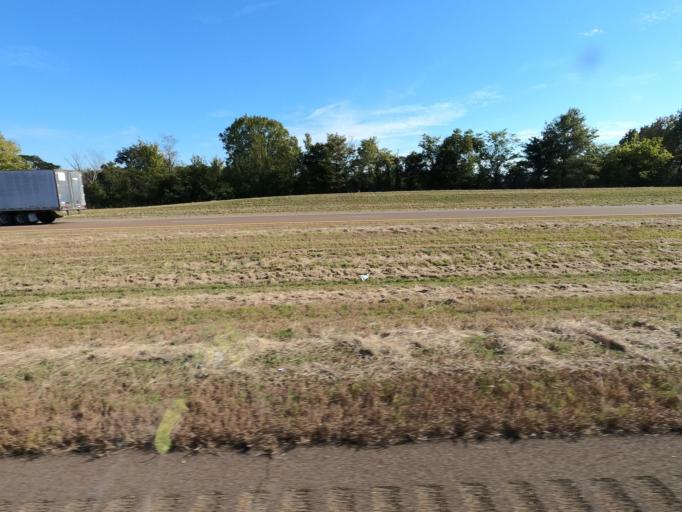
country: US
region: Tennessee
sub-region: Dyer County
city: Newbern
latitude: 36.0857
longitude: -89.3295
